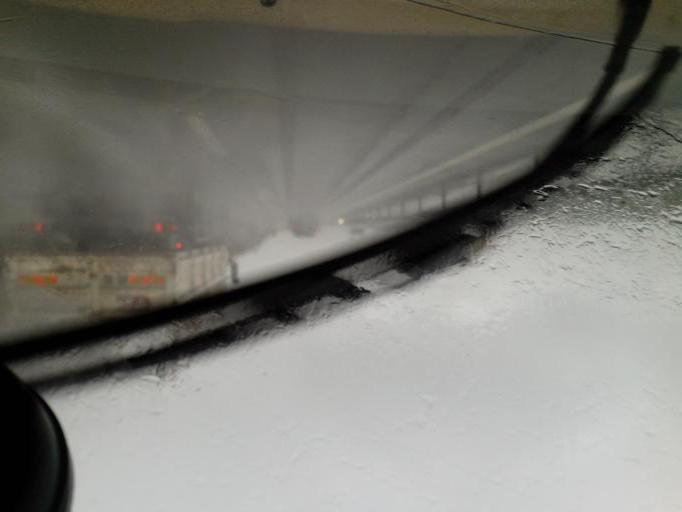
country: FR
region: Brittany
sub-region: Departement d'Ille-et-Vilaine
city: Saint-Gilles
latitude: 48.1629
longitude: -1.8594
